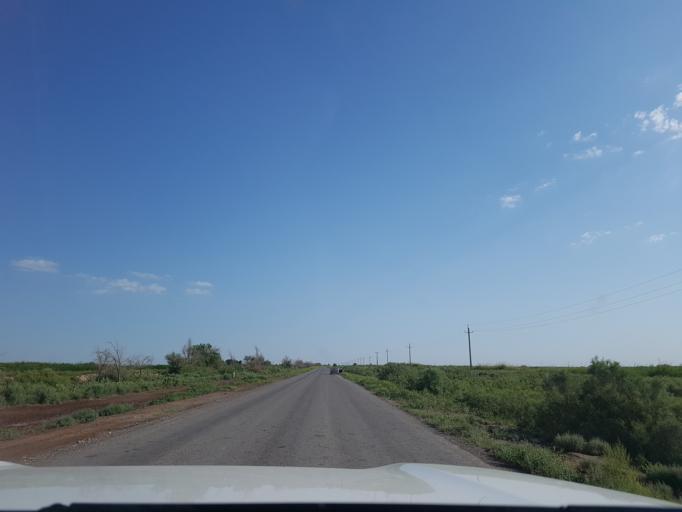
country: TM
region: Dasoguz
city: Koeneuergench
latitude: 41.8866
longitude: 58.7067
